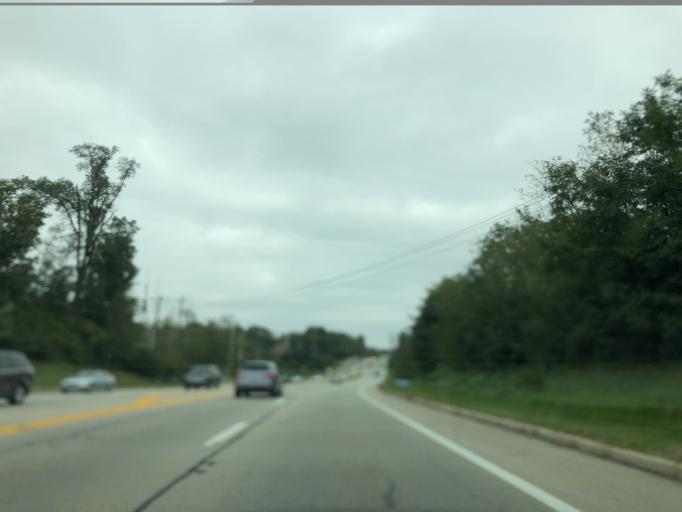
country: US
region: Ohio
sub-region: Hamilton County
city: Sixteen Mile Stand
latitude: 39.2741
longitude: -84.3261
